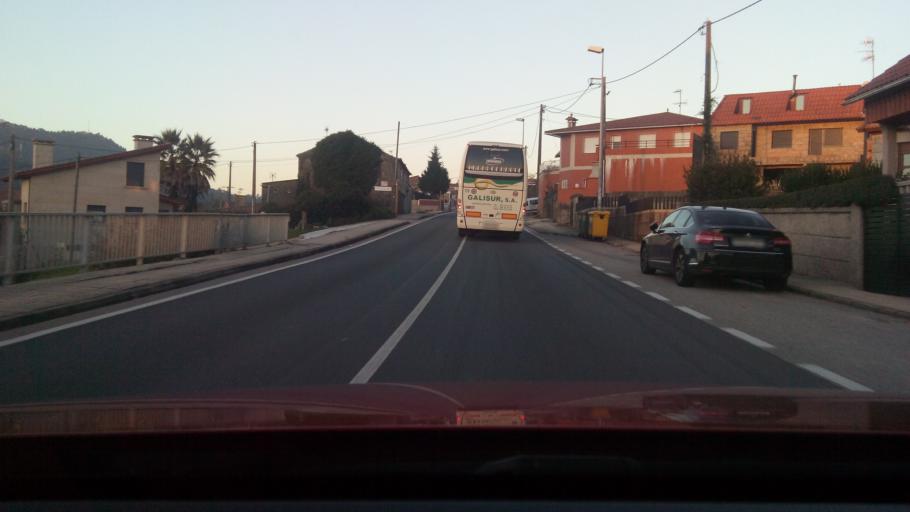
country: ES
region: Galicia
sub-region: Provincia de Pontevedra
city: Gondomar
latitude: 42.1450
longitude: -8.7290
